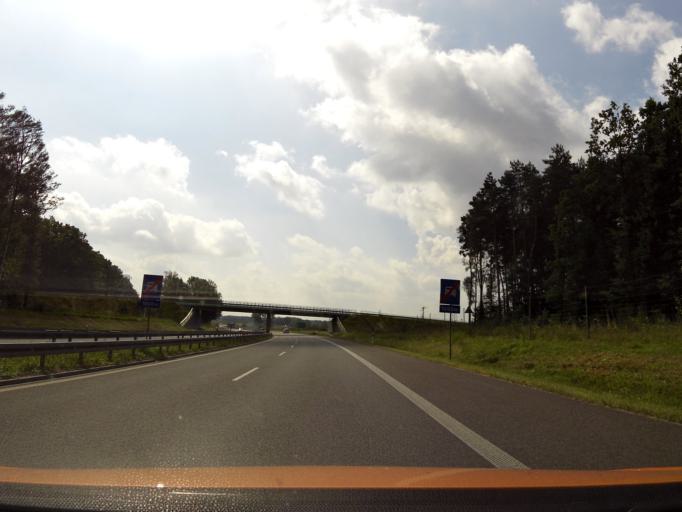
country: PL
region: West Pomeranian Voivodeship
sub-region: Powiat goleniowski
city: Nowogard
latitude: 53.6665
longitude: 15.0760
